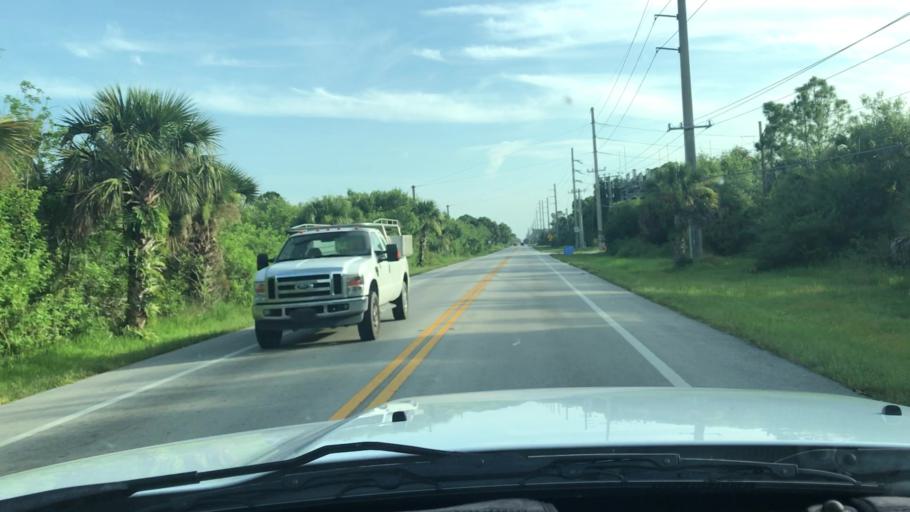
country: US
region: Florida
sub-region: Indian River County
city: Florida Ridge
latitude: 27.5751
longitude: -80.4143
